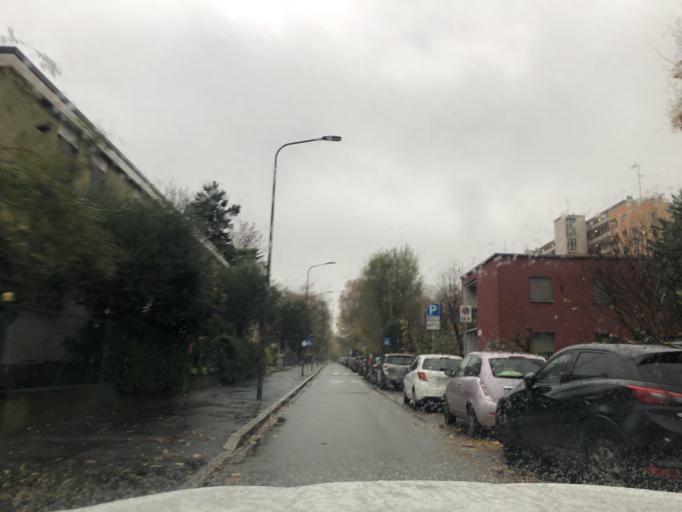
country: IT
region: Lombardy
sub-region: Citta metropolitana di Milano
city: Novate Milanese
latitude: 45.4843
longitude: 9.1351
